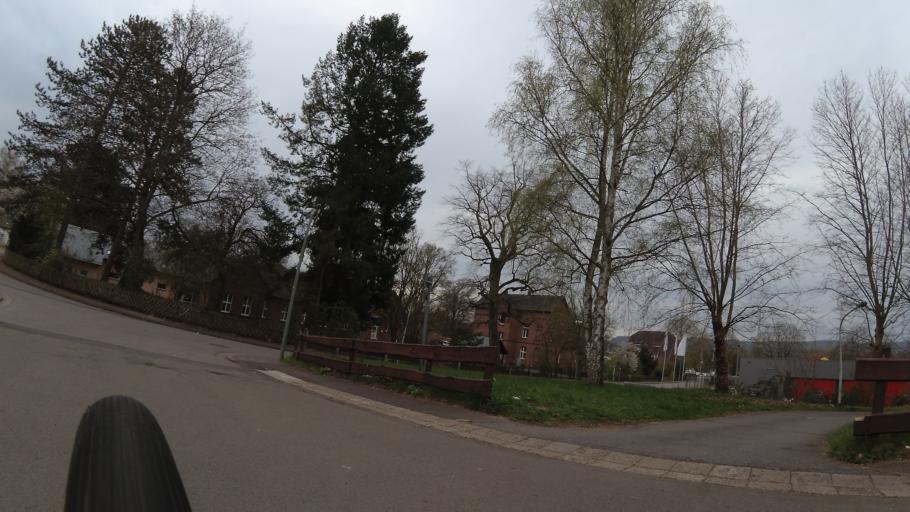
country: DE
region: Saarland
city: Merzig
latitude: 49.4588
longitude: 6.6304
